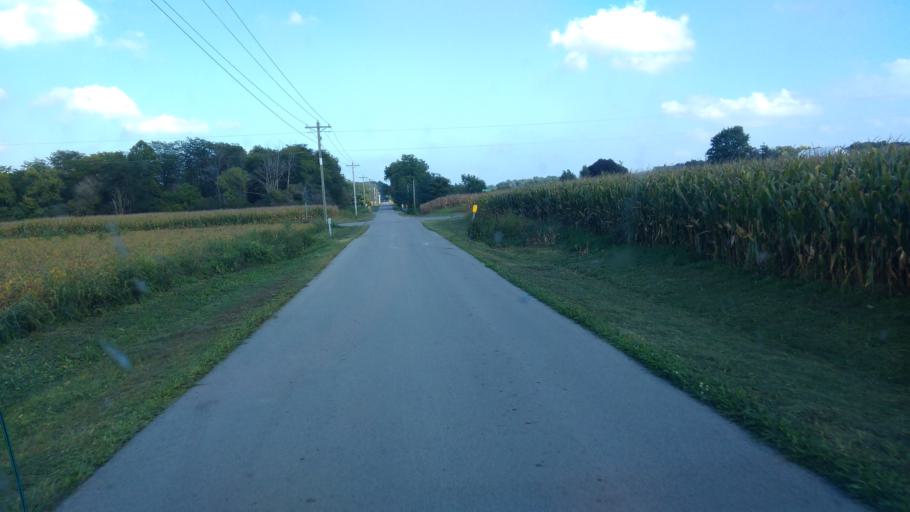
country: US
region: Ohio
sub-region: Hancock County
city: Arlington
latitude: 40.8486
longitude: -83.7093
